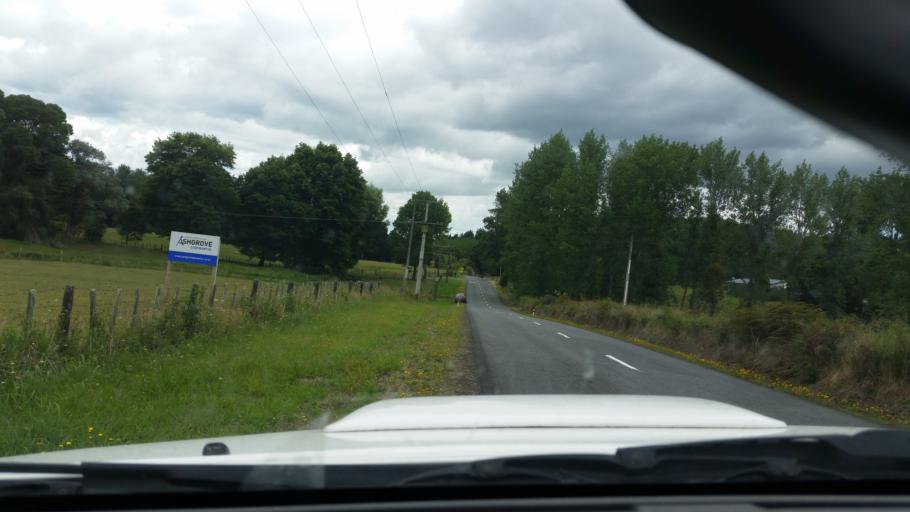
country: NZ
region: Northland
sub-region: Kaipara District
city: Dargaville
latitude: -35.7431
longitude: 173.8768
